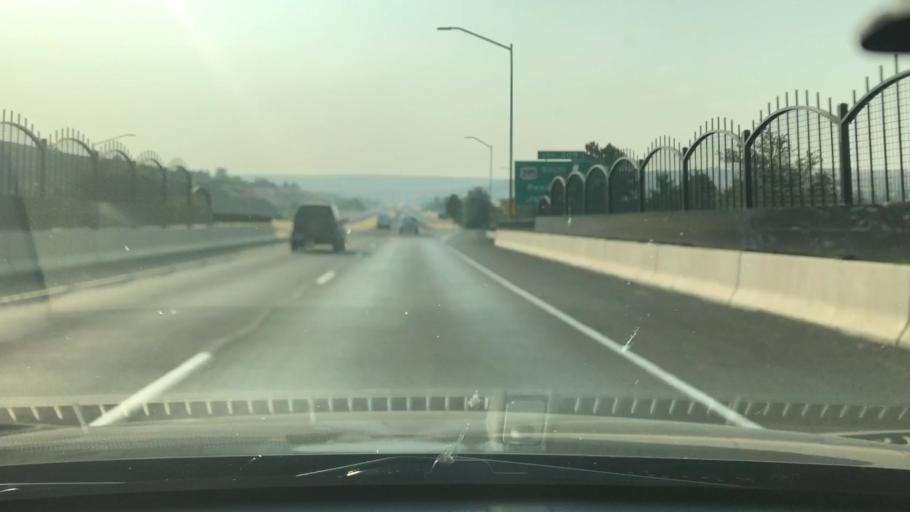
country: US
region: Oregon
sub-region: Umatilla County
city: Pendleton
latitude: 45.6631
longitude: -118.8062
